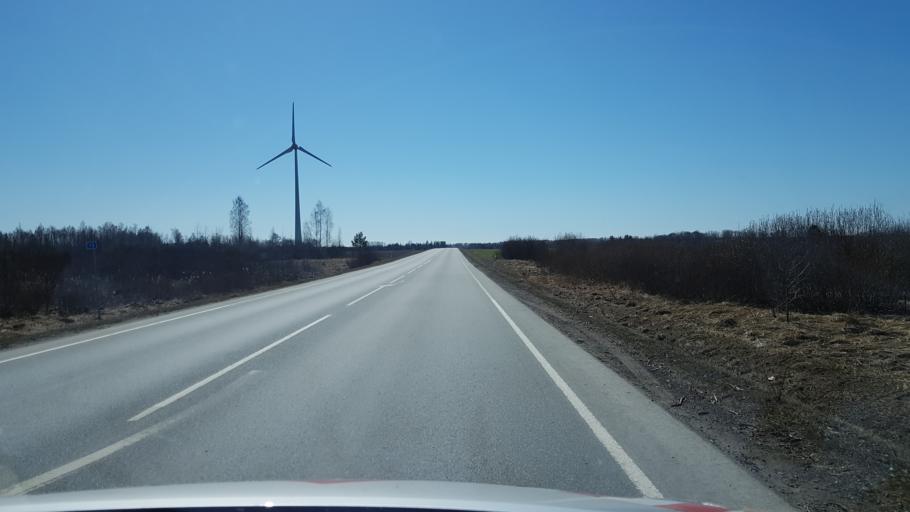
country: EE
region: Laeaene-Virumaa
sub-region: Viru-Nigula vald
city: Kunda
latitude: 59.4912
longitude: 26.5017
